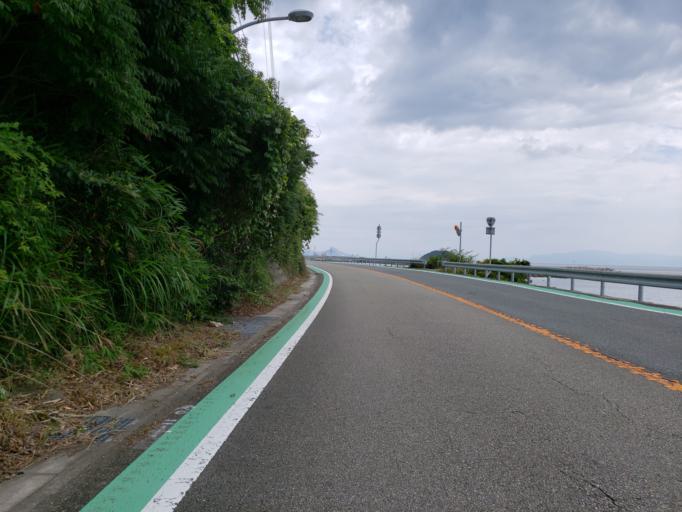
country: JP
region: Hyogo
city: Aioi
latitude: 34.7699
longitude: 134.4698
